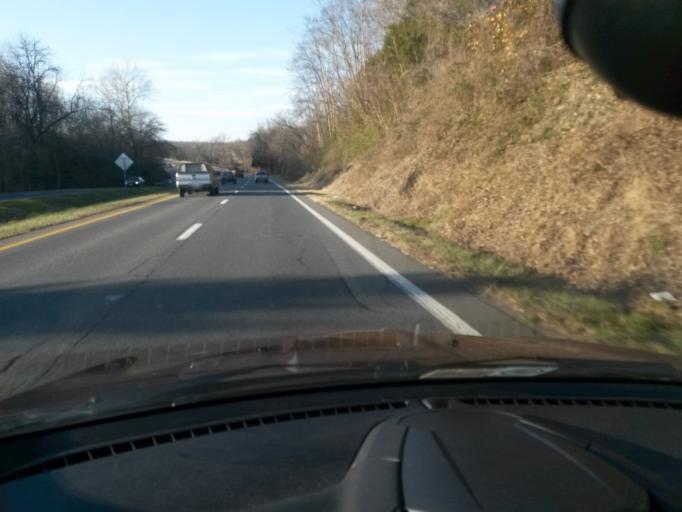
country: US
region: Virginia
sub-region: Amherst County
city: Madison Heights
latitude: 37.3838
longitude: -79.0529
